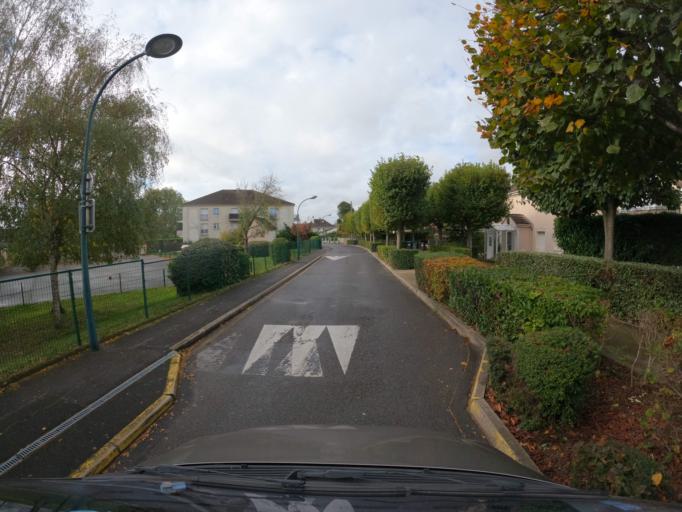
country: FR
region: Ile-de-France
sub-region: Departement de Seine-et-Marne
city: Courtry
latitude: 48.9140
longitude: 2.5965
